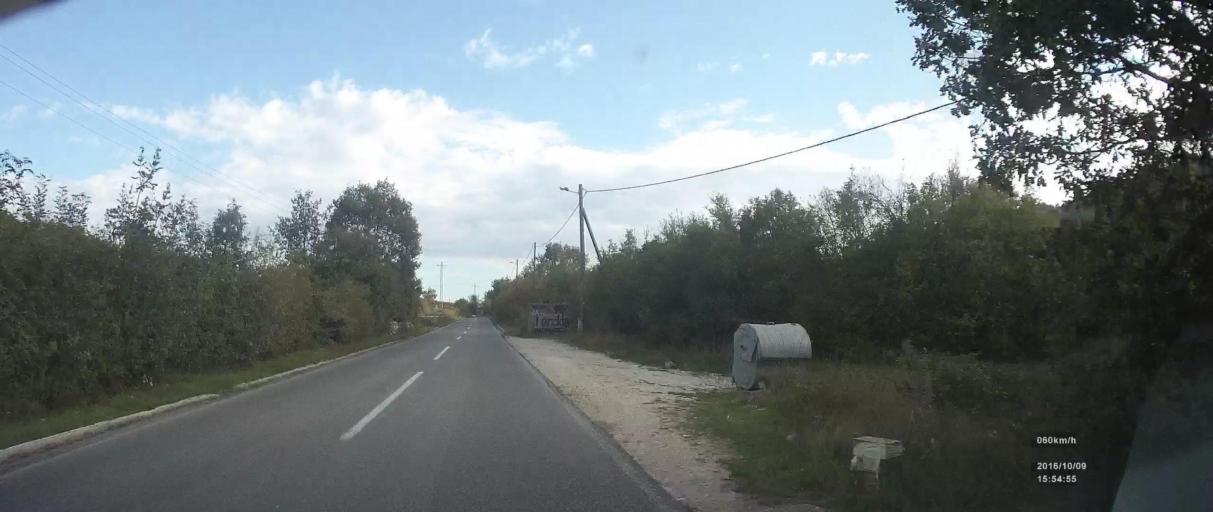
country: HR
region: Splitsko-Dalmatinska
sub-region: Grad Trogir
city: Trogir
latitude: 43.5907
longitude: 16.2268
